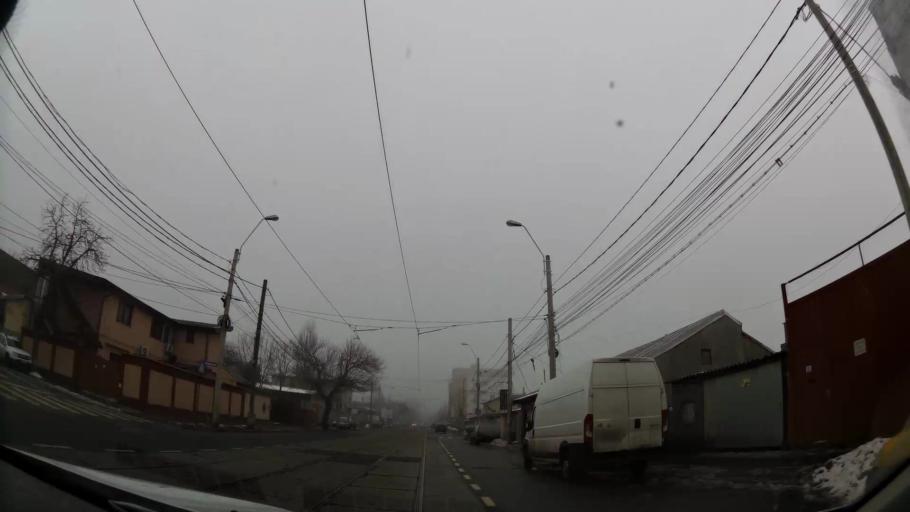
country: RO
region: Ilfov
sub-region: Comuna Chiajna
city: Rosu
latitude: 44.4652
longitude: 26.0380
